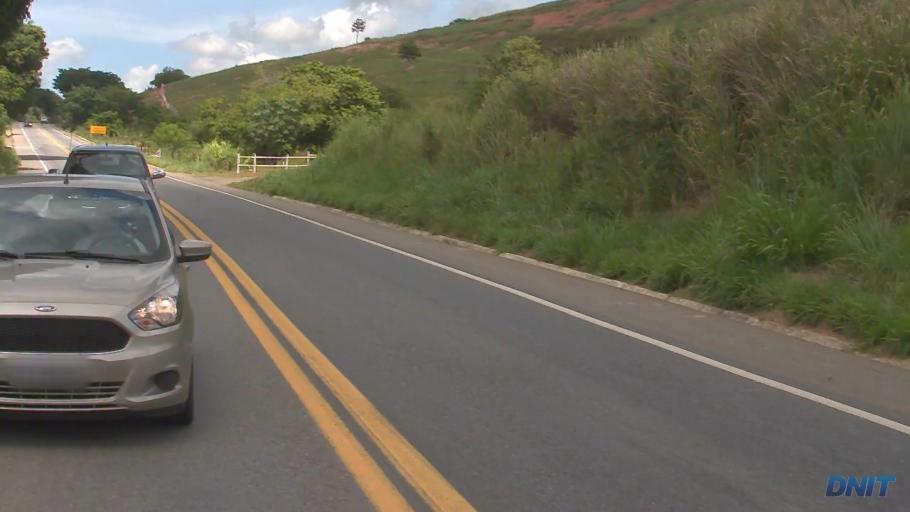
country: BR
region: Minas Gerais
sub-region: Governador Valadares
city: Governador Valadares
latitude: -18.9637
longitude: -42.0789
